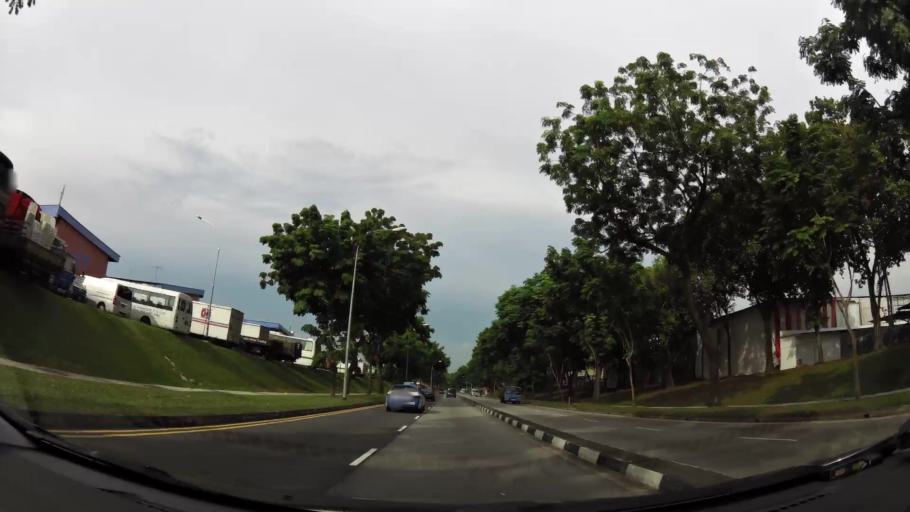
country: SG
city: Singapore
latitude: 1.3531
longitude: 103.8933
